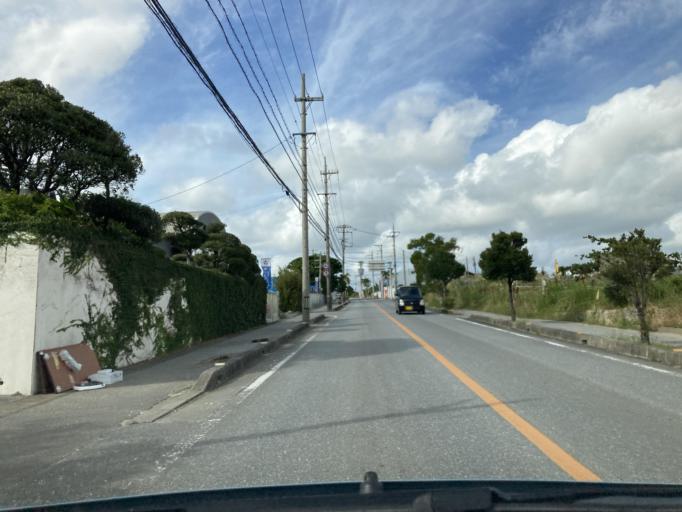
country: JP
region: Okinawa
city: Itoman
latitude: 26.1090
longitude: 127.7200
